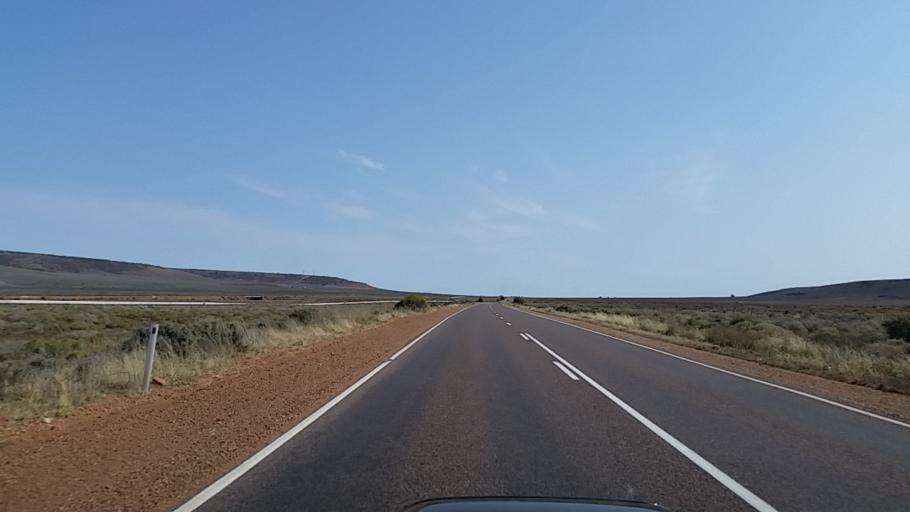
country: AU
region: South Australia
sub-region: Port Augusta
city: Port Augusta West
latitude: -32.5838
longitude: 137.6178
